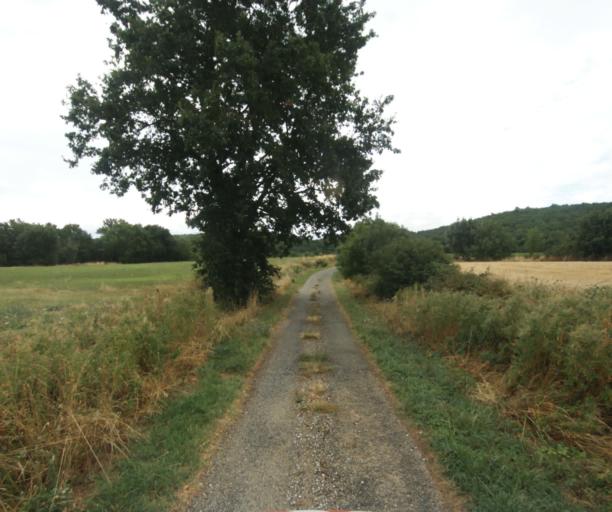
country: FR
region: Midi-Pyrenees
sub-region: Departement de la Haute-Garonne
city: Revel
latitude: 43.4158
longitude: 1.9812
